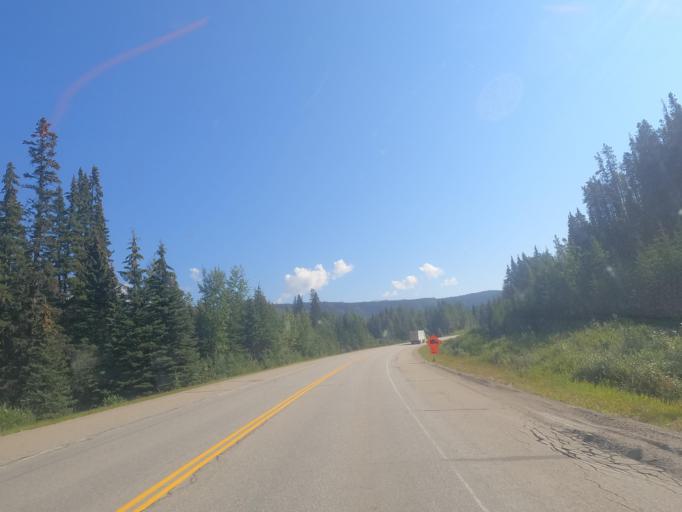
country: CA
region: Alberta
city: Jasper Park Lodge
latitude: 52.8876
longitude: -118.4797
